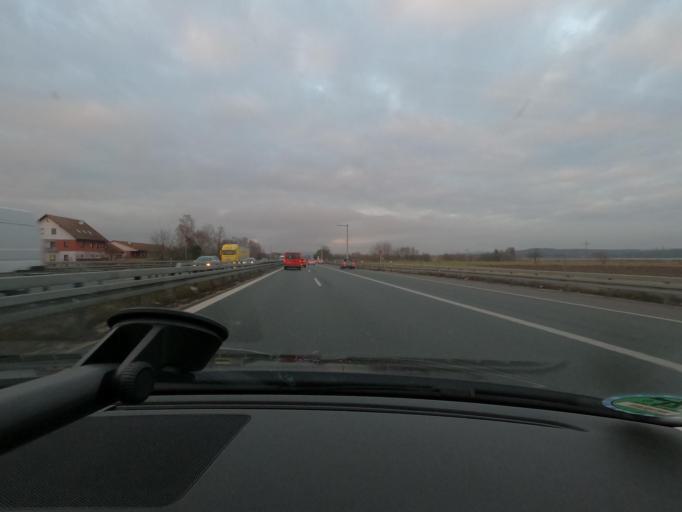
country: DE
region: Bavaria
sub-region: Regierungsbezirk Mittelfranken
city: Baiersdorf
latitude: 49.6710
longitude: 11.0462
